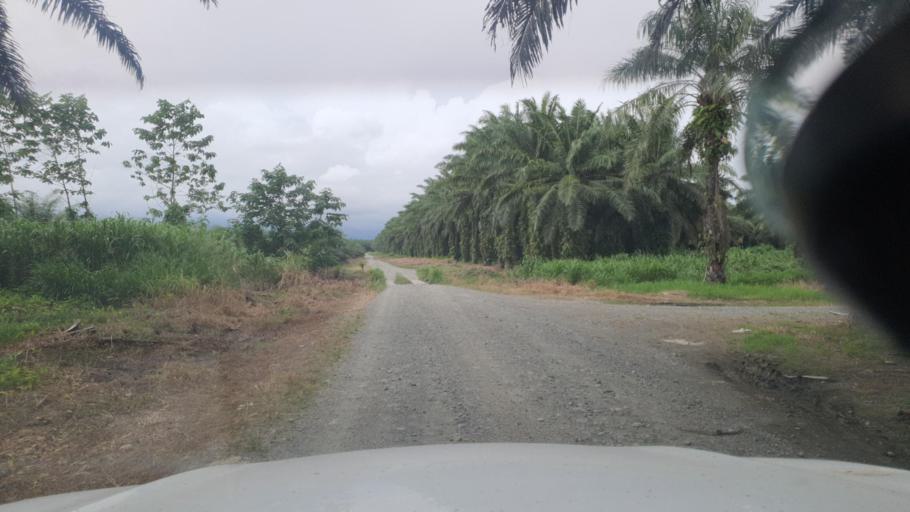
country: SB
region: Guadalcanal
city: Honiara
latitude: -9.4711
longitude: 160.2461
